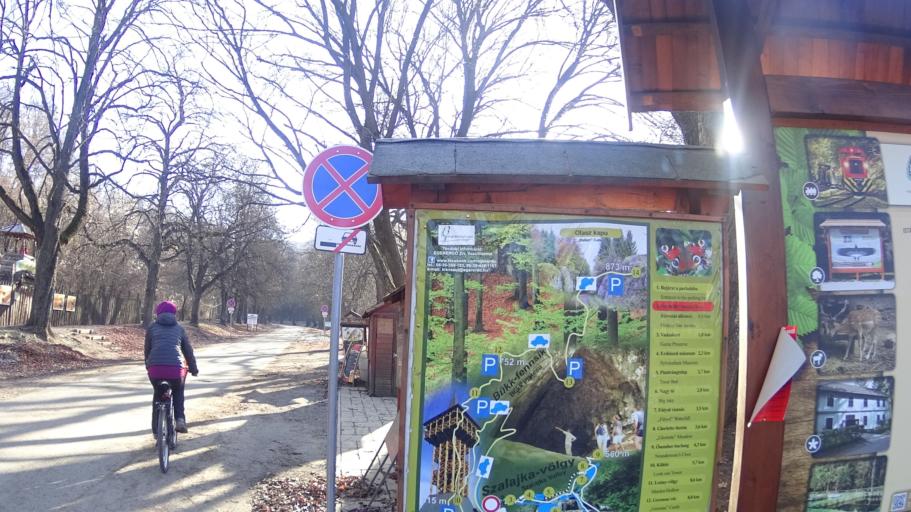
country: HU
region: Heves
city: Szilvasvarad
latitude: 48.0949
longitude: 20.3938
